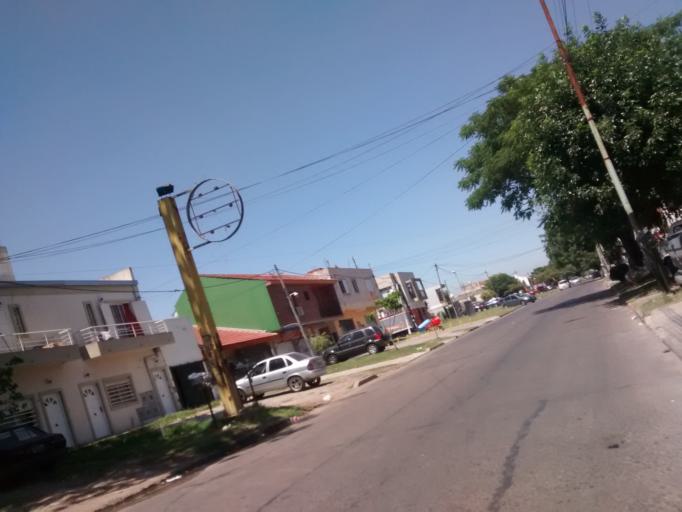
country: AR
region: Buenos Aires
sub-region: Partido de La Plata
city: La Plata
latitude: -34.9339
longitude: -57.9160
